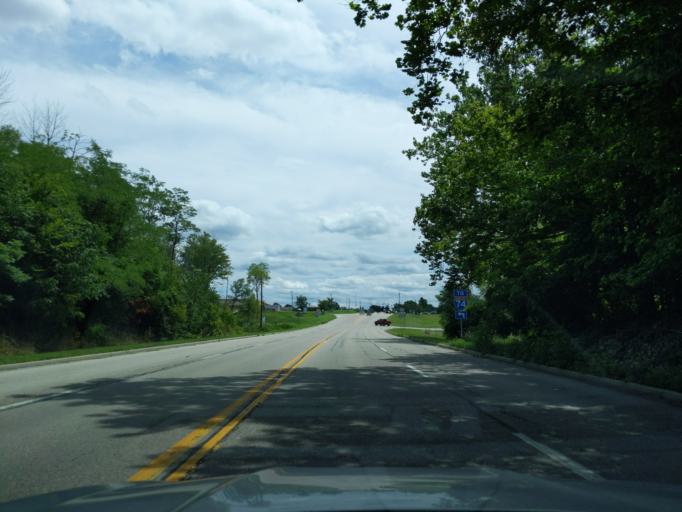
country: US
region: Indiana
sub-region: Ripley County
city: Batesville
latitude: 39.3081
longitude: -85.2214
